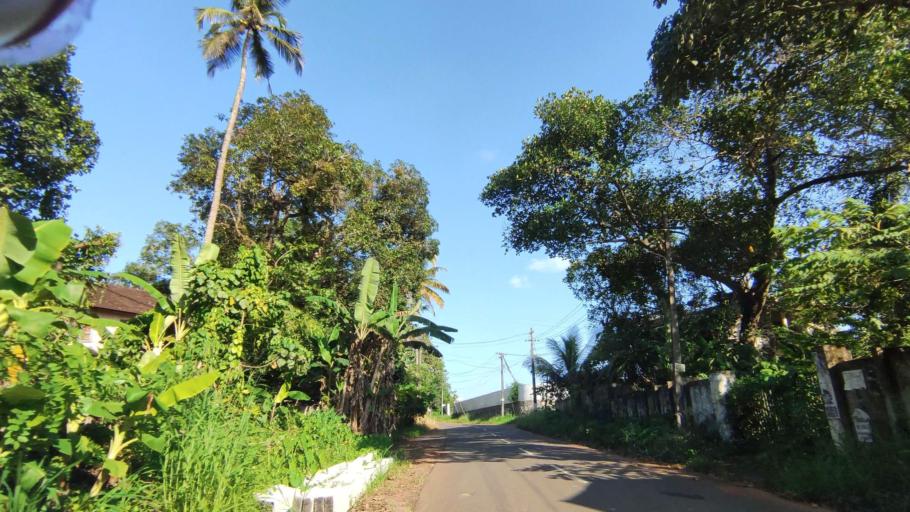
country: IN
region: Kerala
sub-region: Kottayam
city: Kottayam
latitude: 9.5580
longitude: 76.5094
